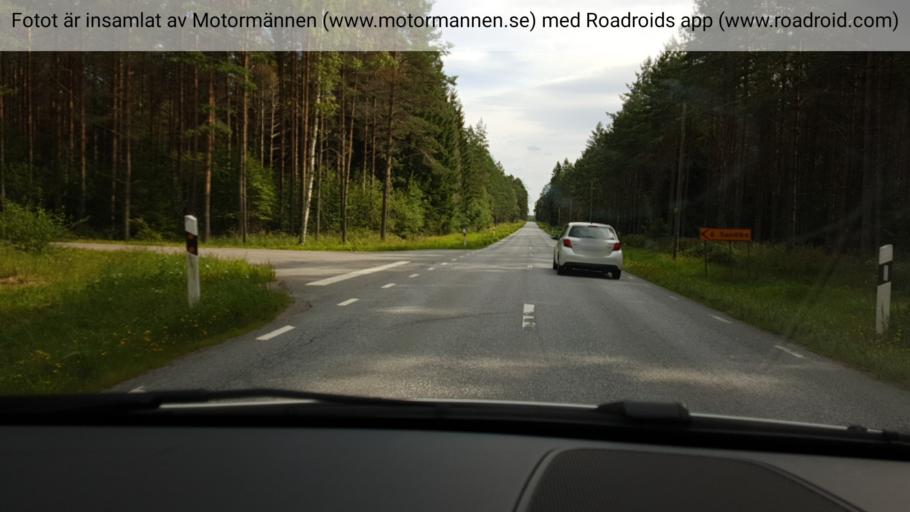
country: SE
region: Uppsala
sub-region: Osthammars Kommun
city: Anneberg
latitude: 60.1937
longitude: 18.3821
